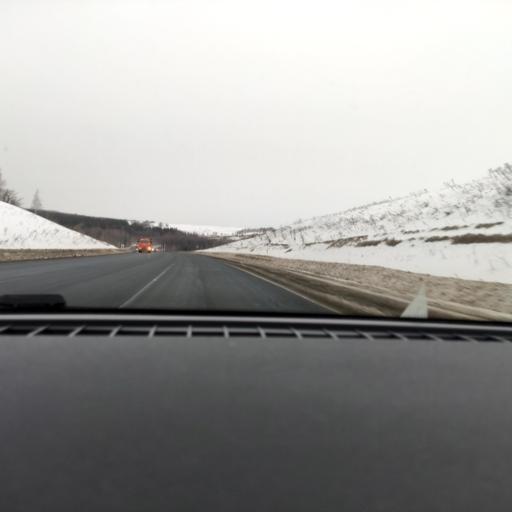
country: RU
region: Samara
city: Novosemeykino
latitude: 53.3544
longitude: 50.4476
